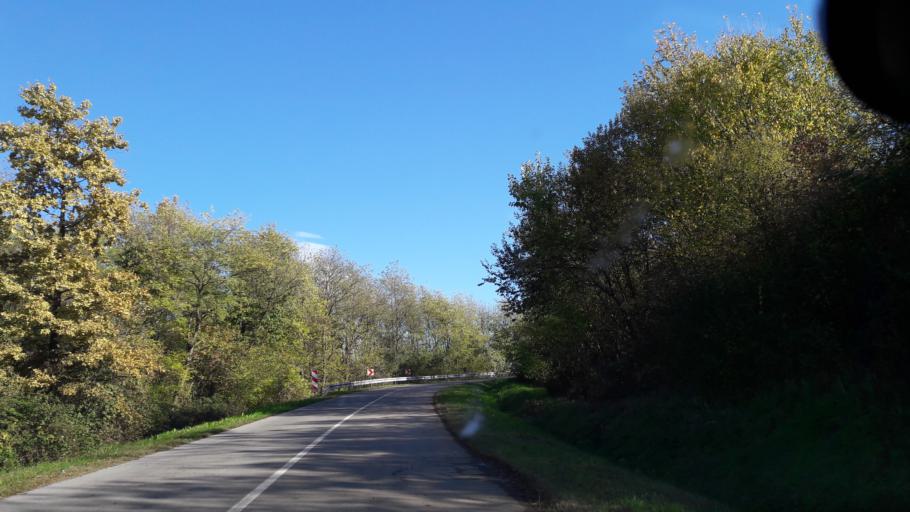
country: HR
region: Osjecko-Baranjska
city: Gorjani
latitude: 45.3847
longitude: 18.2506
